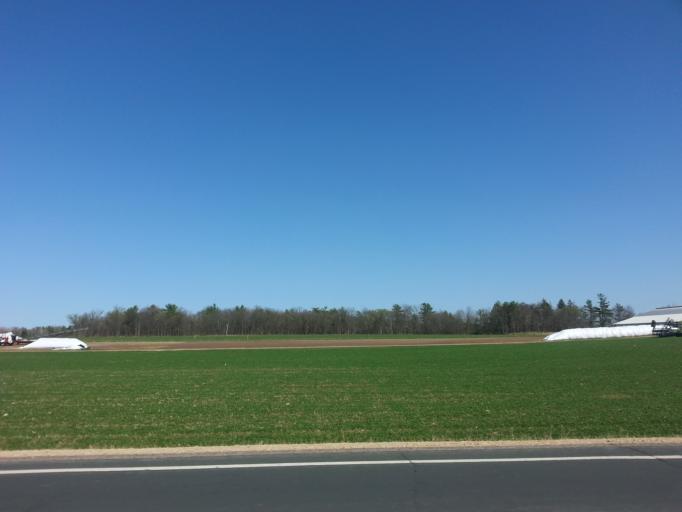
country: US
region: Wisconsin
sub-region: Pepin County
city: Durand
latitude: 44.6869
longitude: -91.9487
